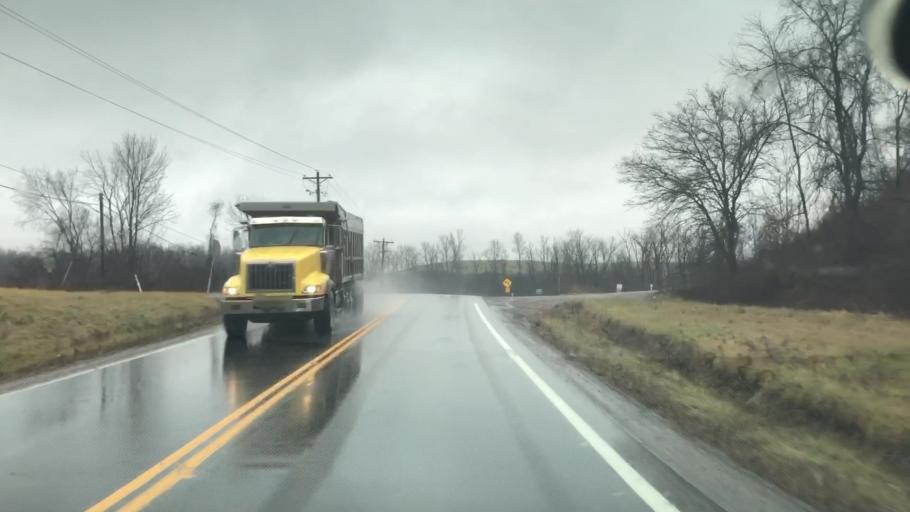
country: US
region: Ohio
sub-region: Harrison County
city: Cadiz
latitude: 40.2207
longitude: -81.0012
